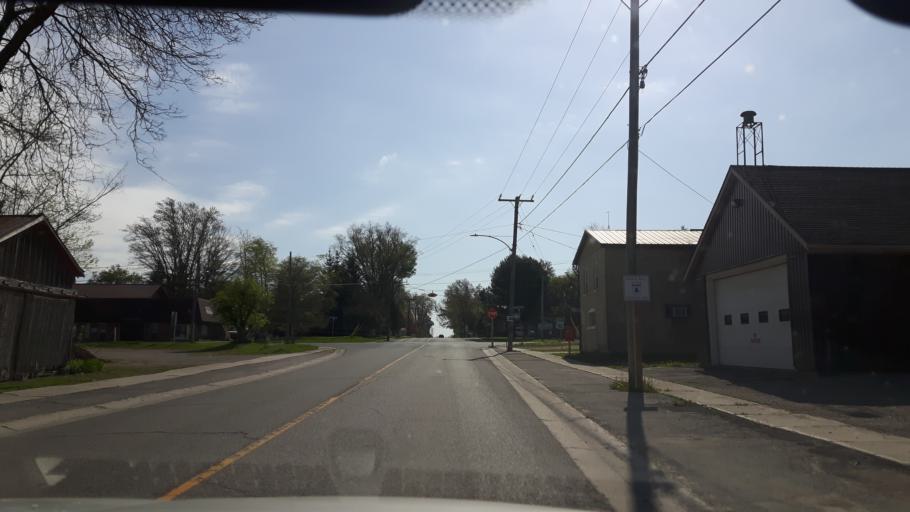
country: CA
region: Ontario
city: Bluewater
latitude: 43.5255
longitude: -81.5183
